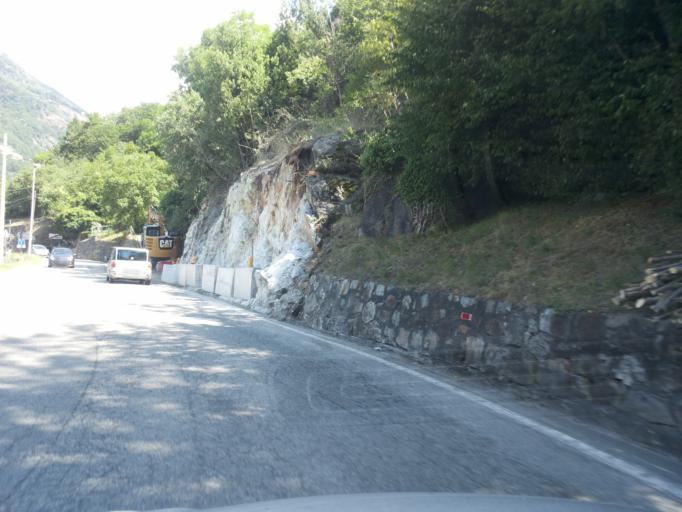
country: IT
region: Aosta Valley
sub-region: Valle d'Aosta
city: Pont-Saint-Martin
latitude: 45.5949
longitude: 7.8035
